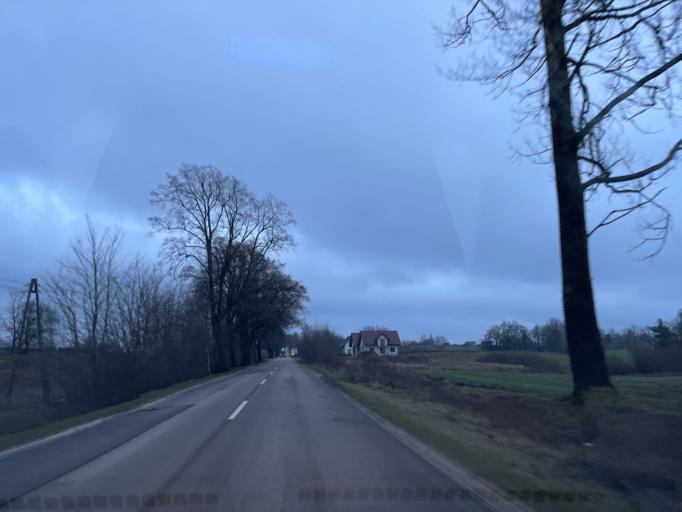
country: PL
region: Pomeranian Voivodeship
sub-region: Powiat kartuski
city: Kartuzy
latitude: 54.4068
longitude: 18.2139
